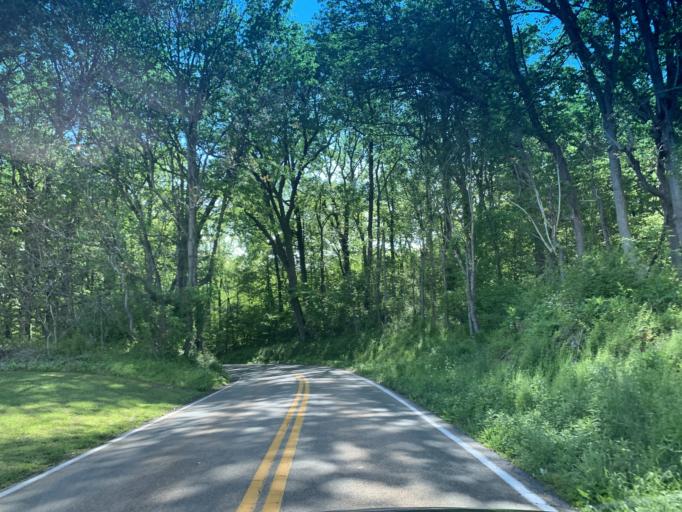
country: US
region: Maryland
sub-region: Cecil County
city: Rising Sun
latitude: 39.6932
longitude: -76.1444
